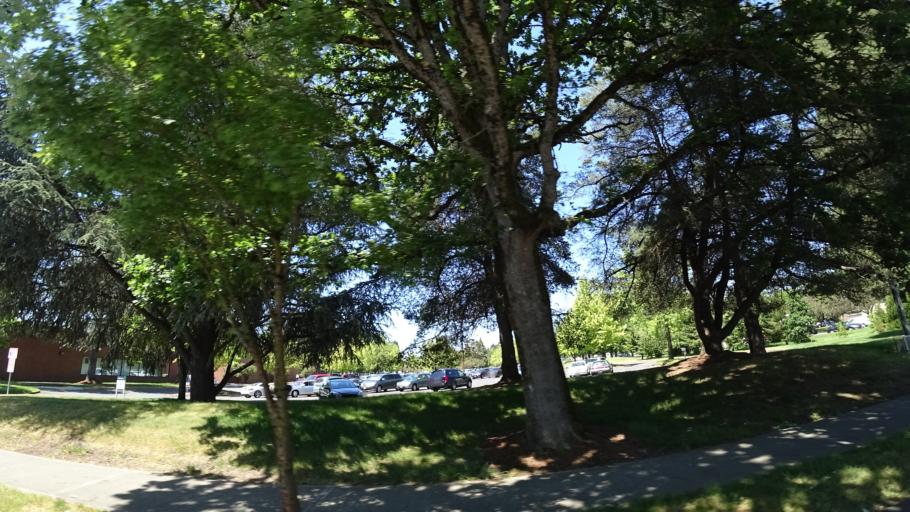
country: US
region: Oregon
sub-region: Washington County
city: Cedar Hills
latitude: 45.5000
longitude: -122.8135
